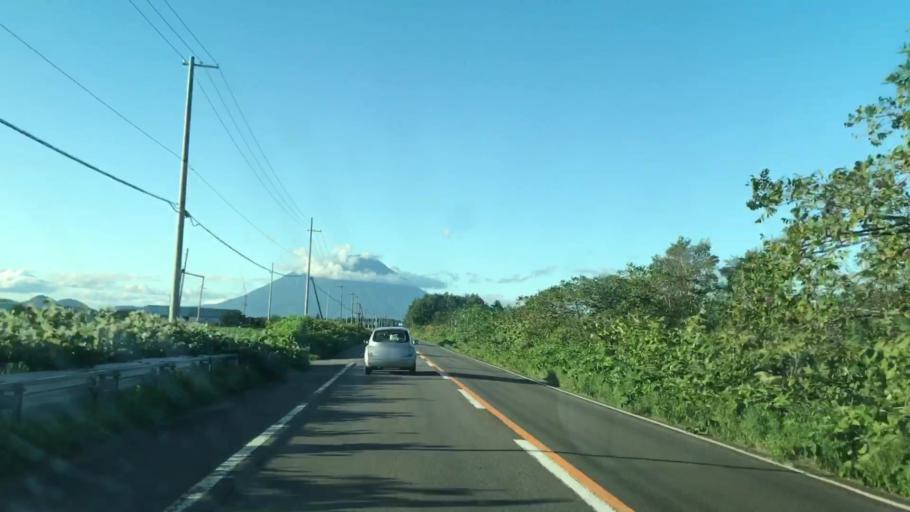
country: JP
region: Hokkaido
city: Niseko Town
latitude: 42.6516
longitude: 140.8111
